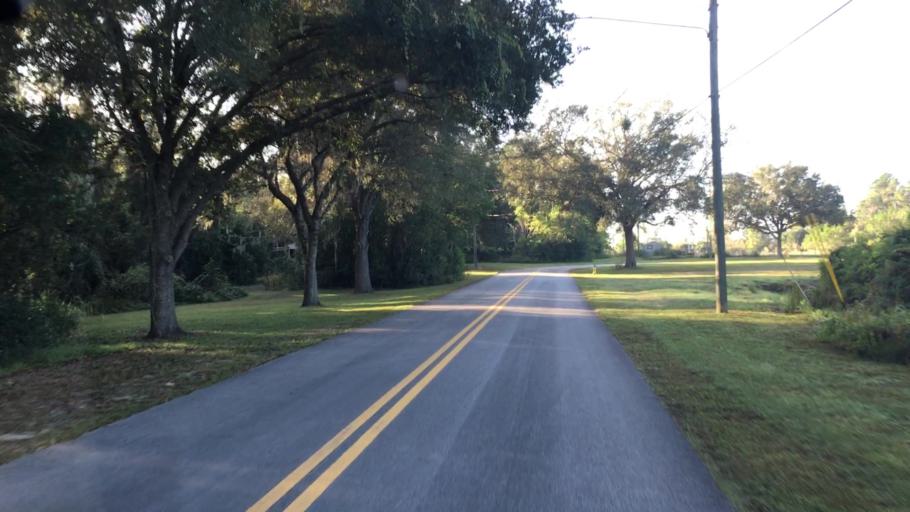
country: US
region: Florida
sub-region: Volusia County
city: North DeLand
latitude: 29.0748
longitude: -81.2754
